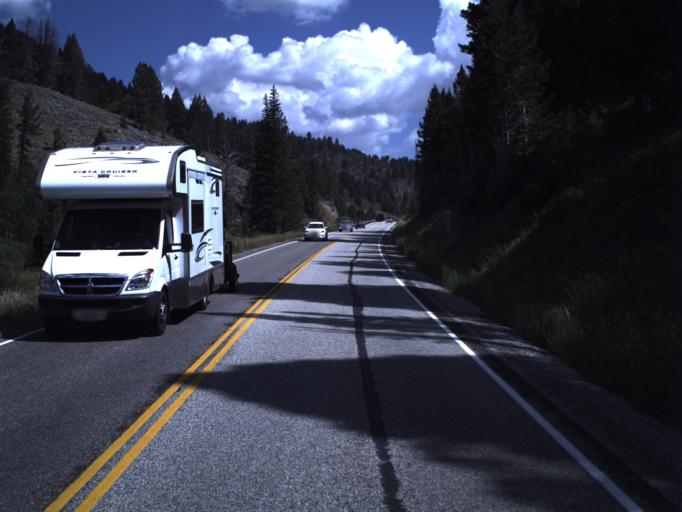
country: US
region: Utah
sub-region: Cache County
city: Richmond
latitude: 41.9514
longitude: -111.5444
